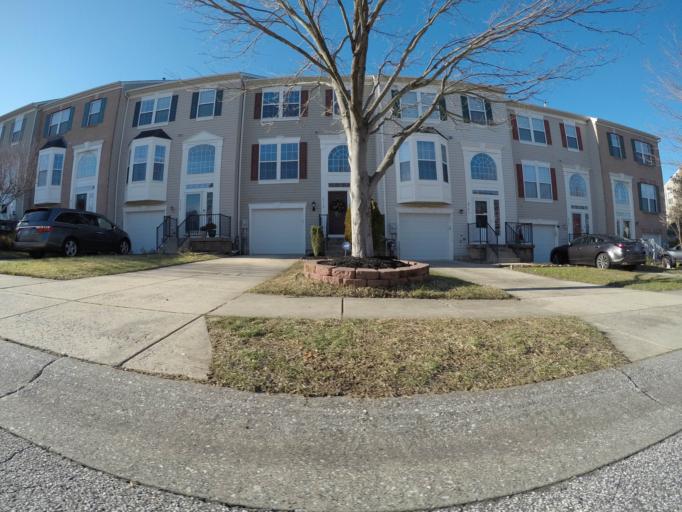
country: US
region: Maryland
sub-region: Howard County
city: Ellicott City
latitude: 39.3036
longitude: -76.8164
